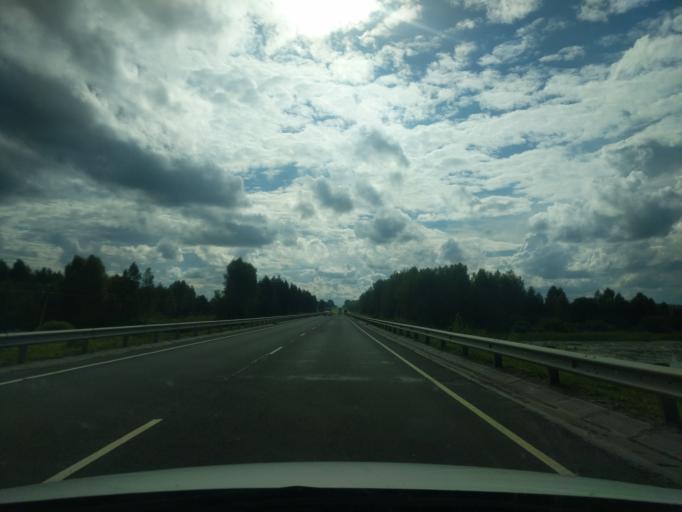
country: RU
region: Jaroslavl
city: Nekrasovskoye
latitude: 57.6293
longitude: 40.3734
